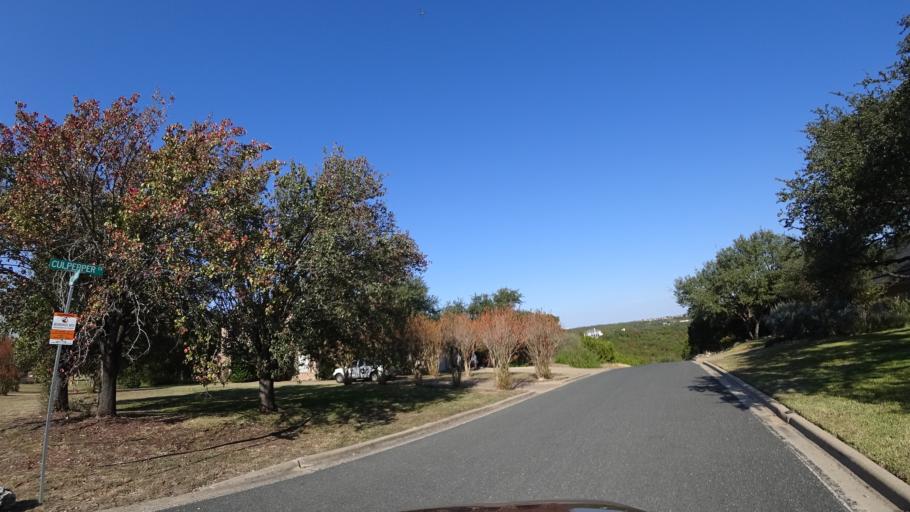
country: US
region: Texas
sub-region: Williamson County
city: Anderson Mill
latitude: 30.3771
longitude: -97.8235
